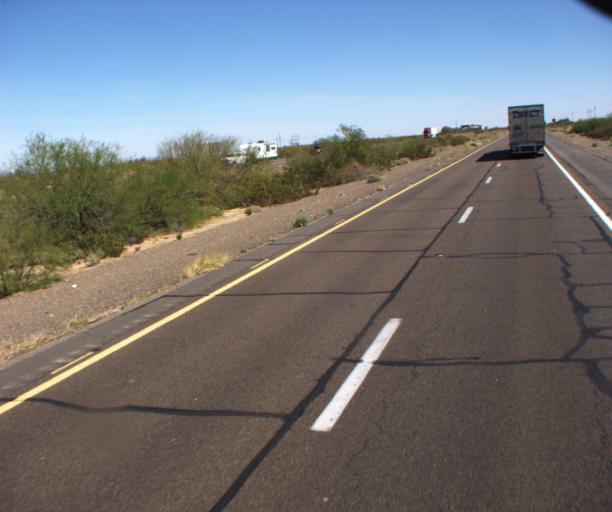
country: US
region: Arizona
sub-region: Yuma County
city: Wellton
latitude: 32.8220
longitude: -113.4615
